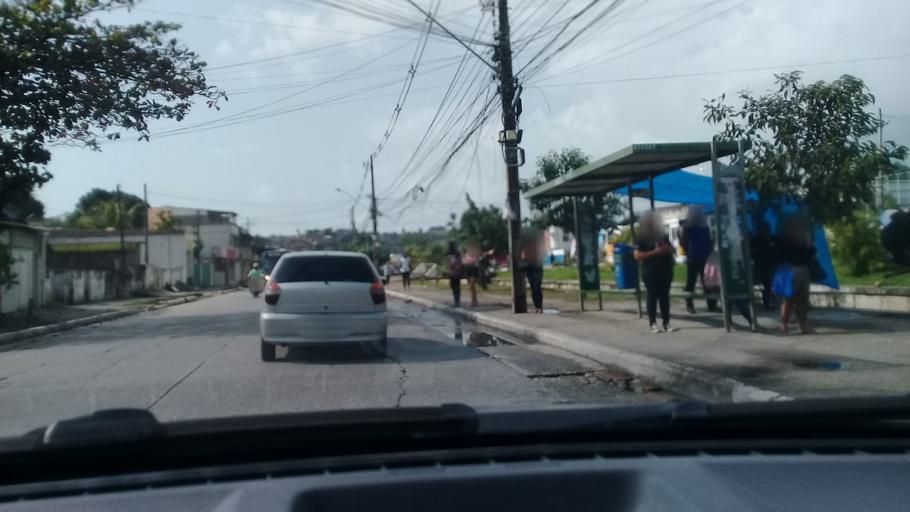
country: BR
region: Pernambuco
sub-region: Jaboatao Dos Guararapes
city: Jaboatao
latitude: -8.1387
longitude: -34.9358
